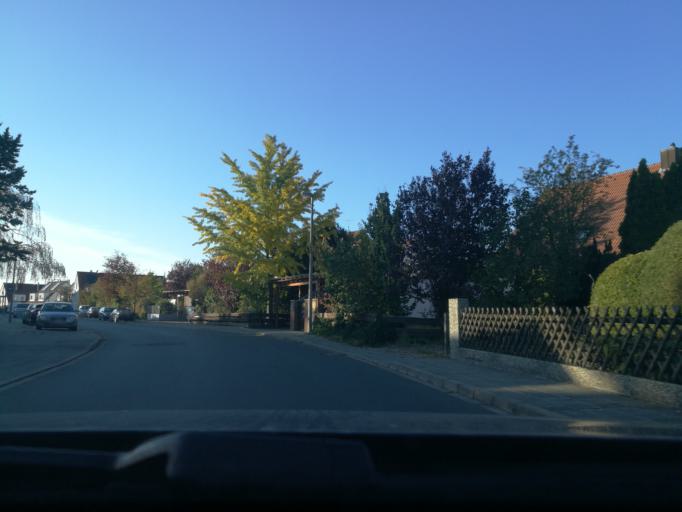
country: DE
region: Bavaria
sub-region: Regierungsbezirk Mittelfranken
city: Erlangen
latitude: 49.5331
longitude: 11.0191
